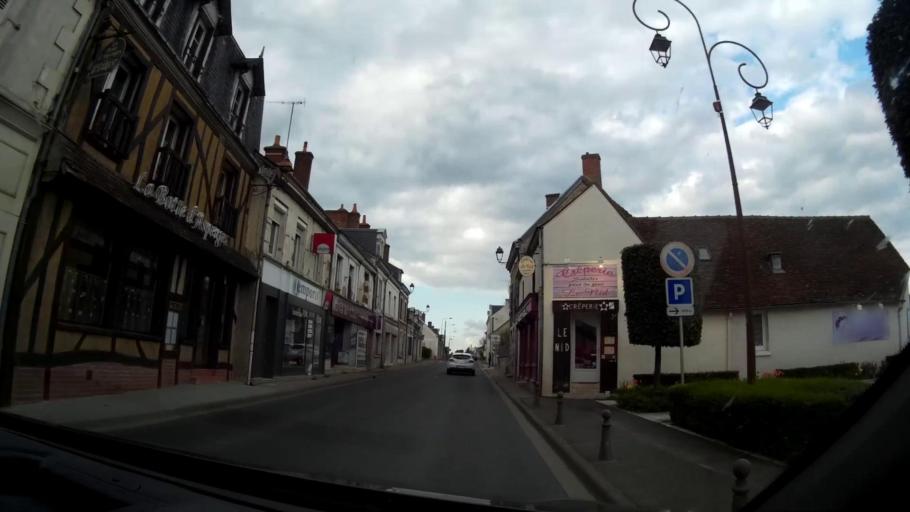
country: FR
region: Centre
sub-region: Departement du Loir-et-Cher
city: Contres
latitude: 47.4195
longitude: 1.4287
